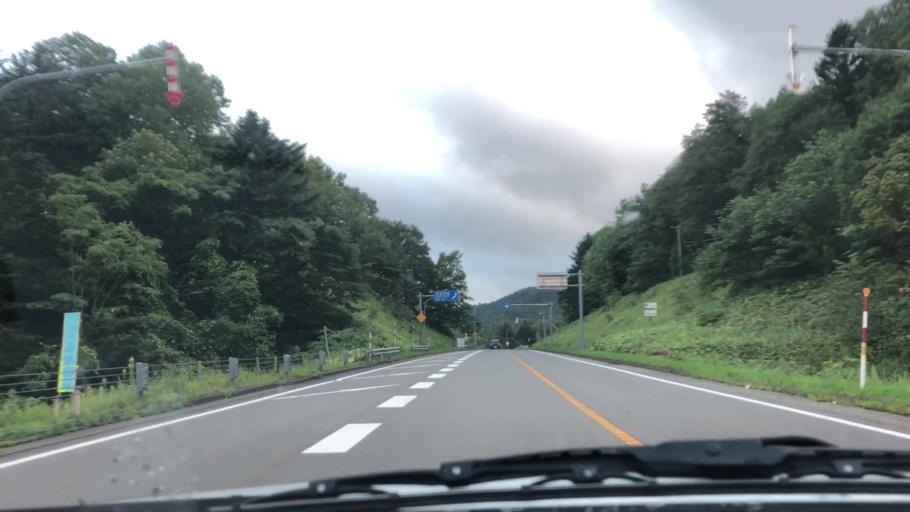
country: JP
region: Hokkaido
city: Shimo-furano
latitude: 42.9109
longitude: 142.3607
